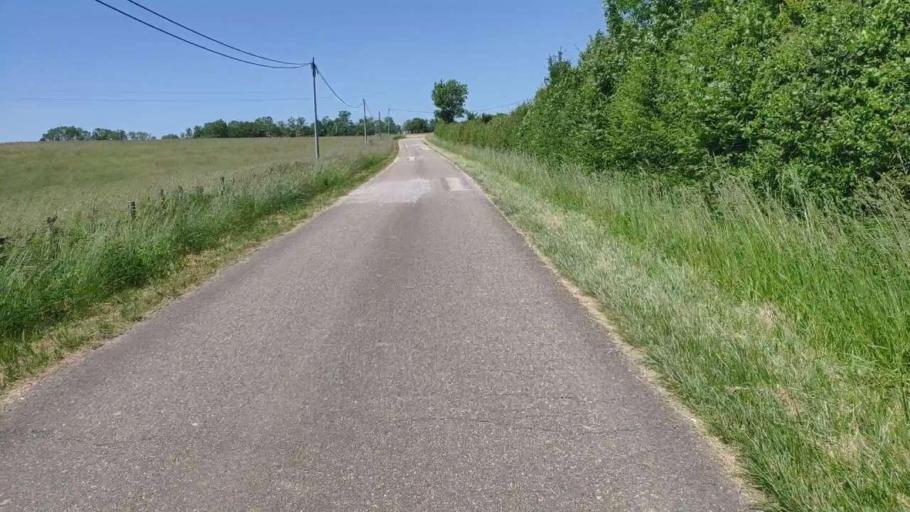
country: FR
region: Franche-Comte
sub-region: Departement du Jura
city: Bletterans
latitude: 46.7529
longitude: 5.4250
